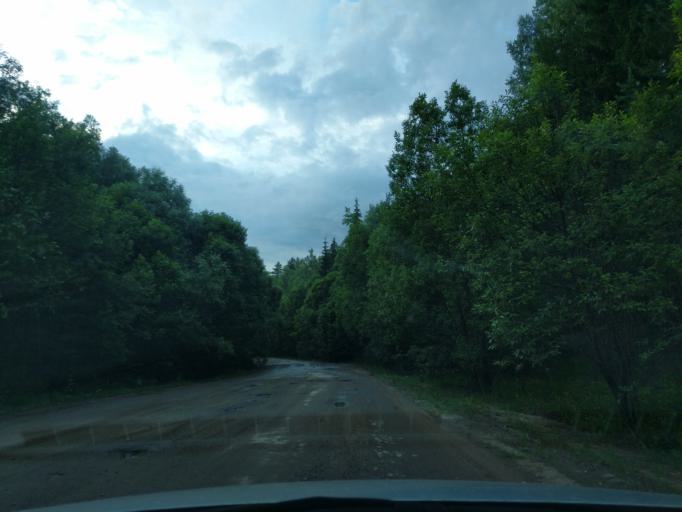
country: RU
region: Kaluga
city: Myatlevo
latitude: 54.8459
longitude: 35.6163
